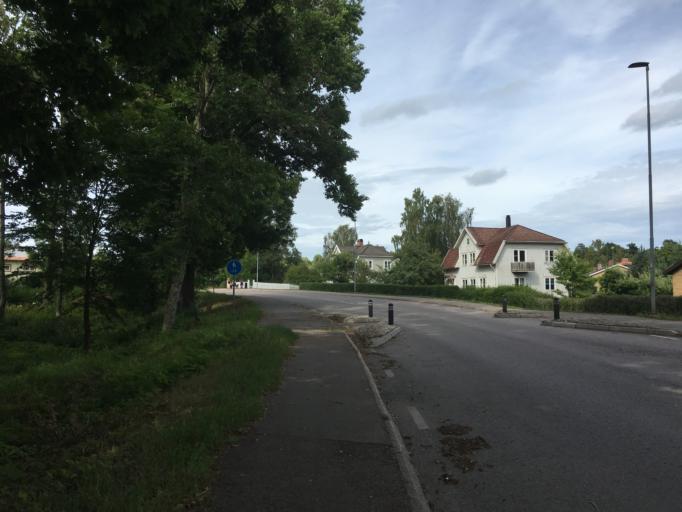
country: SE
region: Kalmar
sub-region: Nybro Kommun
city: Nybro
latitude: 56.9400
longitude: 15.9146
